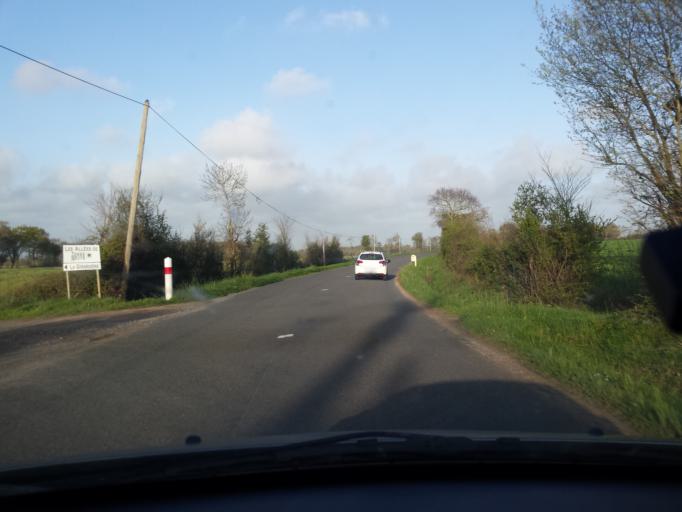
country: FR
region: Pays de la Loire
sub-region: Departement de la Vendee
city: Vaire
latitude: 46.5703
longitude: -1.7591
